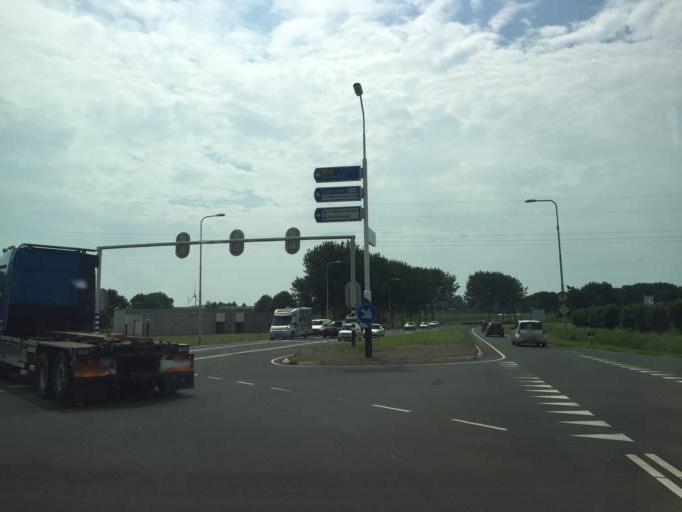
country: NL
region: North Holland
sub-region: Gemeente Enkhuizen
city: Enkhuizen
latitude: 52.6960
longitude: 5.2740
